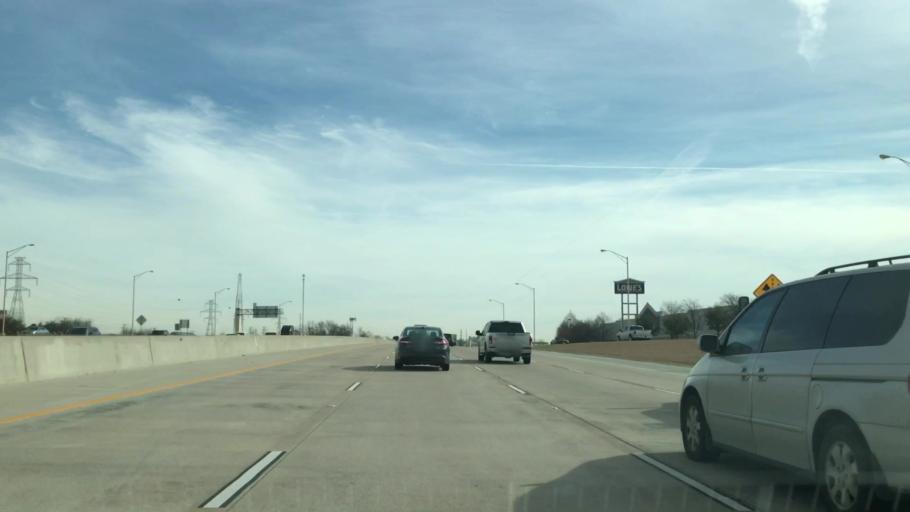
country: US
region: Texas
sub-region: Dallas County
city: Addison
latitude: 33.0121
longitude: -96.7933
